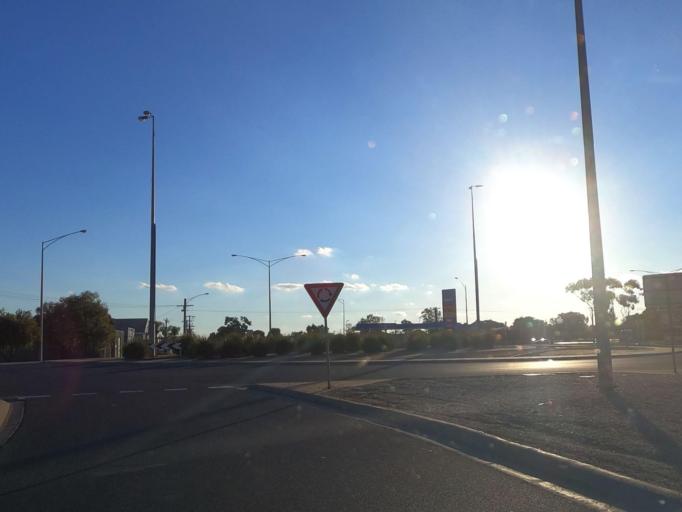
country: AU
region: Victoria
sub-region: Swan Hill
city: Swan Hill
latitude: -35.3274
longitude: 143.5536
